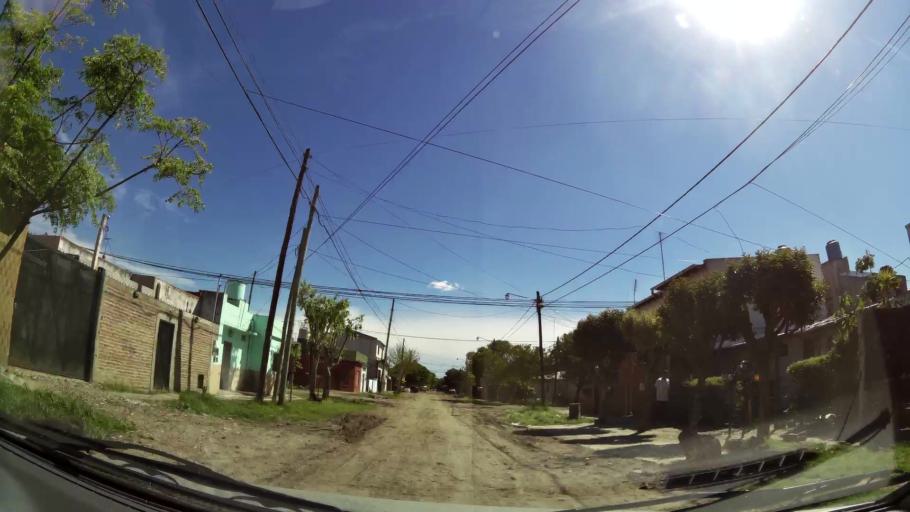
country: AR
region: Buenos Aires
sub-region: Partido de Almirante Brown
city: Adrogue
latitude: -34.7829
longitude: -58.3468
